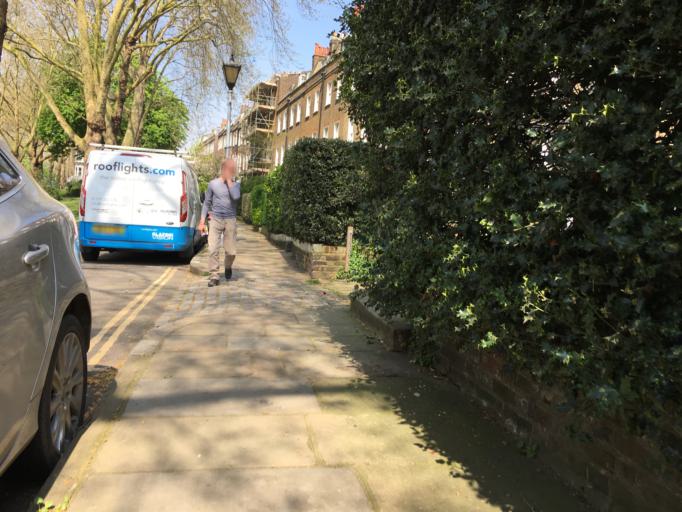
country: GB
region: England
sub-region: Greater London
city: Camden Town
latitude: 51.5575
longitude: -0.1469
